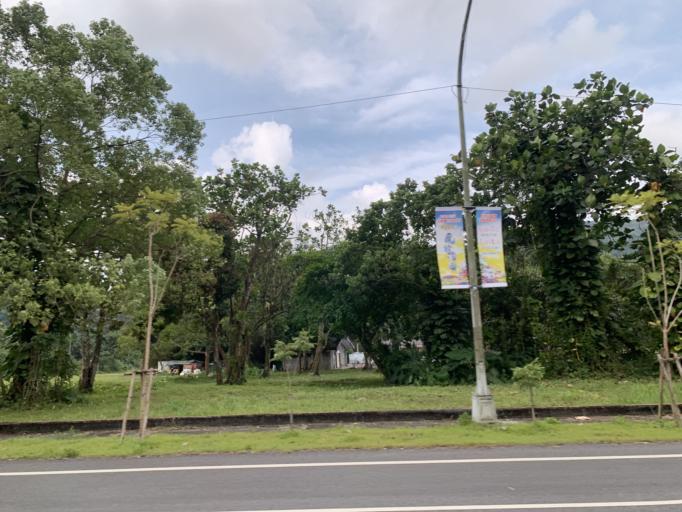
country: TW
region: Taiwan
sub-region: Hualien
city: Hualian
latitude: 23.9353
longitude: 121.5061
